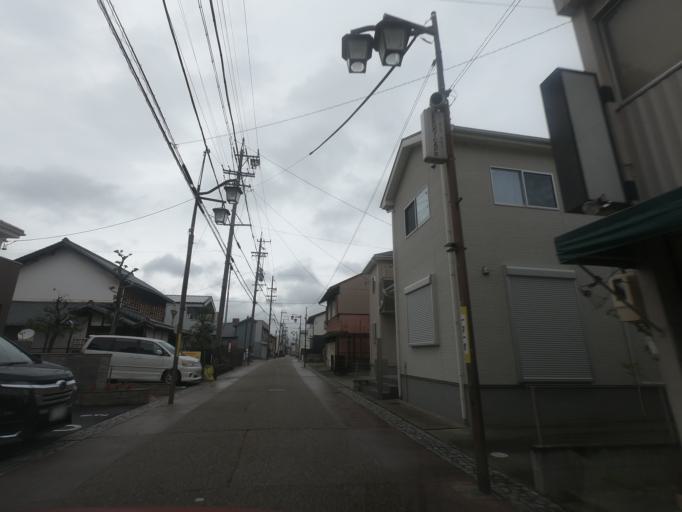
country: JP
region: Aichi
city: Kasugai
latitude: 35.2478
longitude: 136.9782
